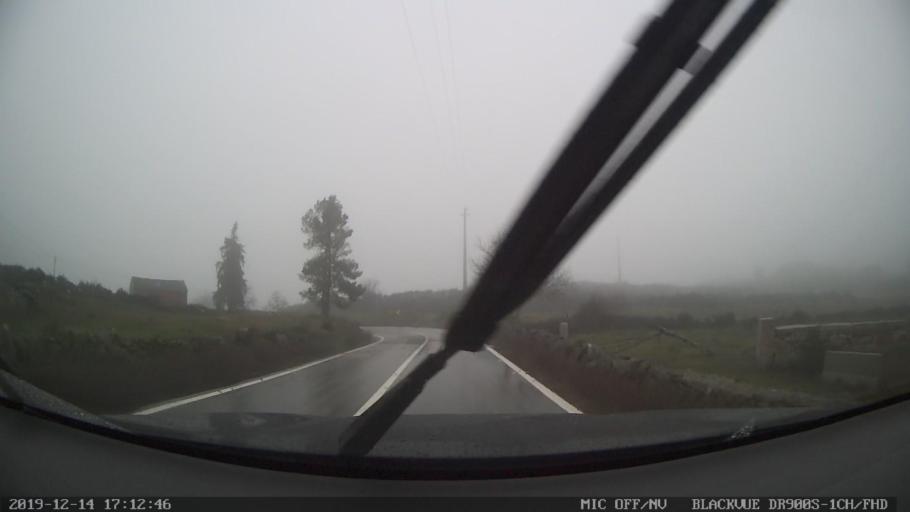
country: PT
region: Vila Real
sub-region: Vila Pouca de Aguiar
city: Vila Pouca de Aguiar
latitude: 41.4962
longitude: -7.6219
